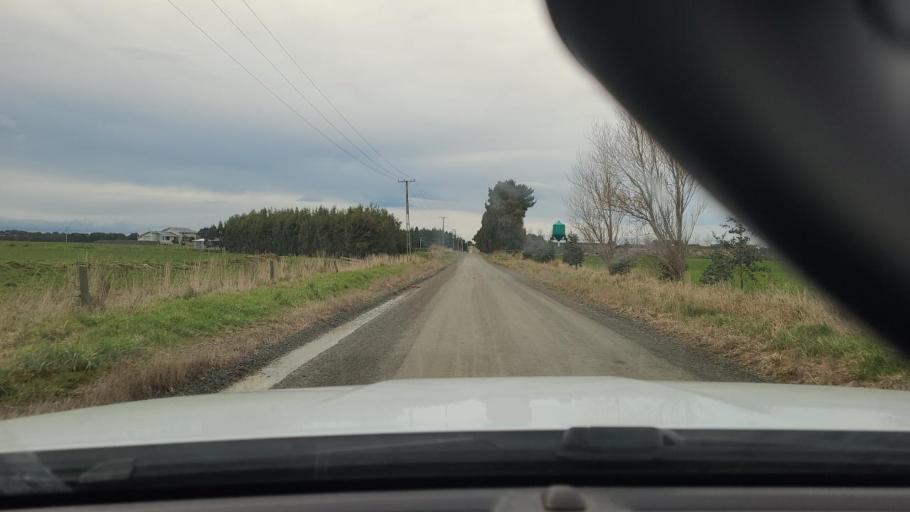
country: NZ
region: Southland
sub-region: Invercargill City
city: Invercargill
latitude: -46.3297
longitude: 168.3214
